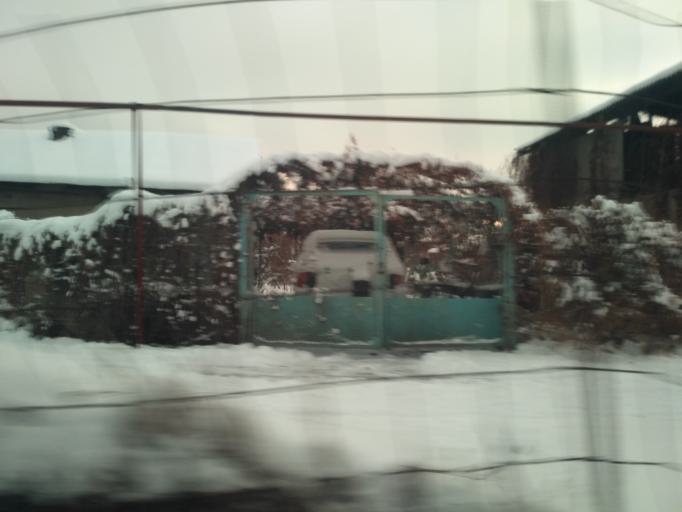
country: KZ
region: Almaty Qalasy
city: Almaty
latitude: 43.2117
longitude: 76.7813
